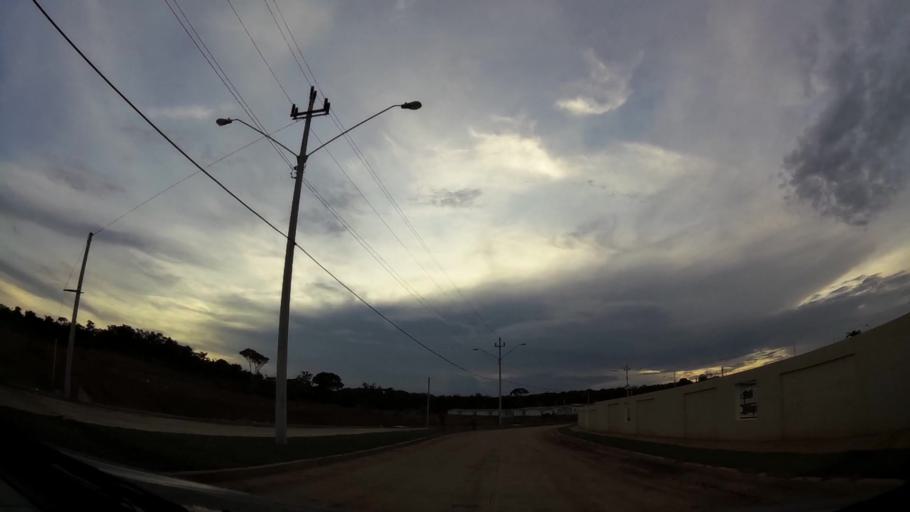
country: PA
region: Panama
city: La Mitra
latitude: 8.8560
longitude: -79.7562
